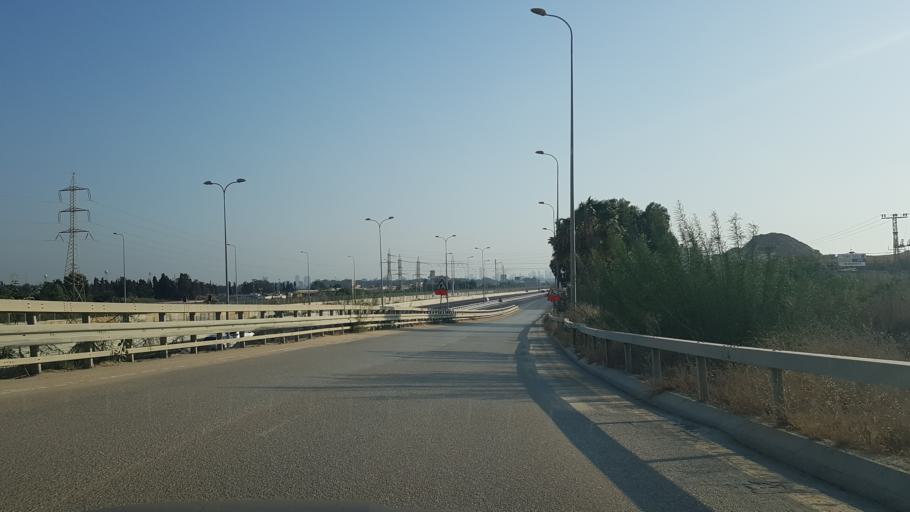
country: IL
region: Tel Aviv
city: Herzliyya
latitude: 32.1602
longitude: 34.8152
